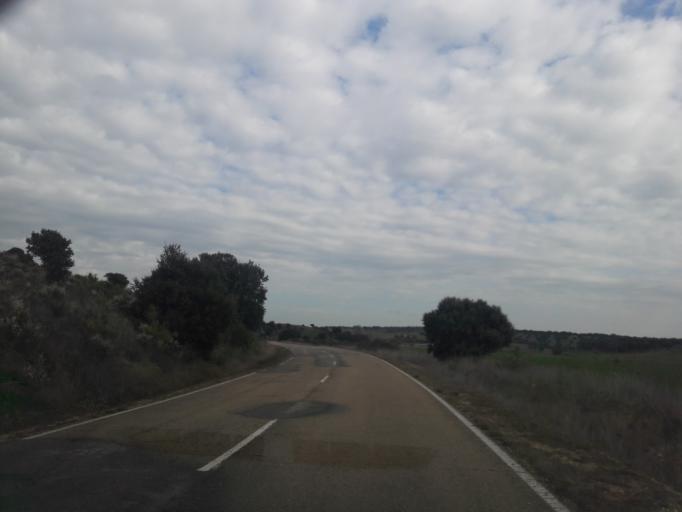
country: ES
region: Castille and Leon
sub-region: Provincia de Salamanca
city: Pastores
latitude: 40.5385
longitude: -6.5273
